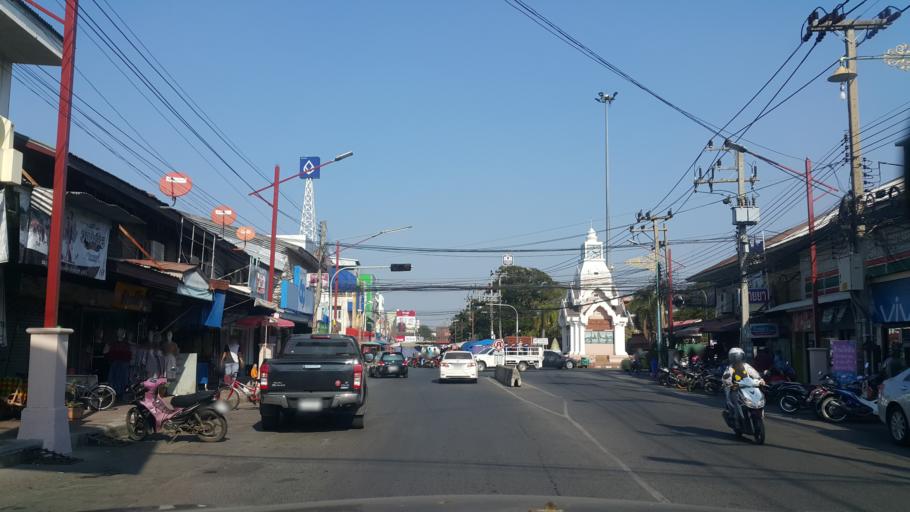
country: TH
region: Nakhon Ratchasima
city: Phimai
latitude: 15.2190
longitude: 102.4953
